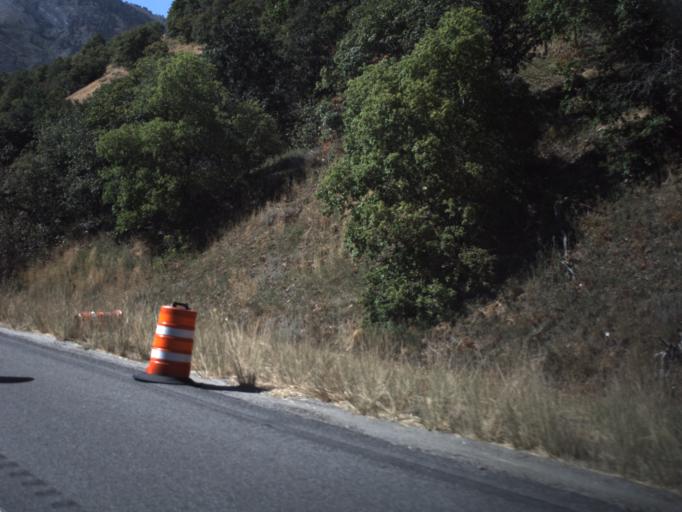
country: US
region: Utah
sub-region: Cache County
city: Wellsville
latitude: 41.6050
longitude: -111.9728
